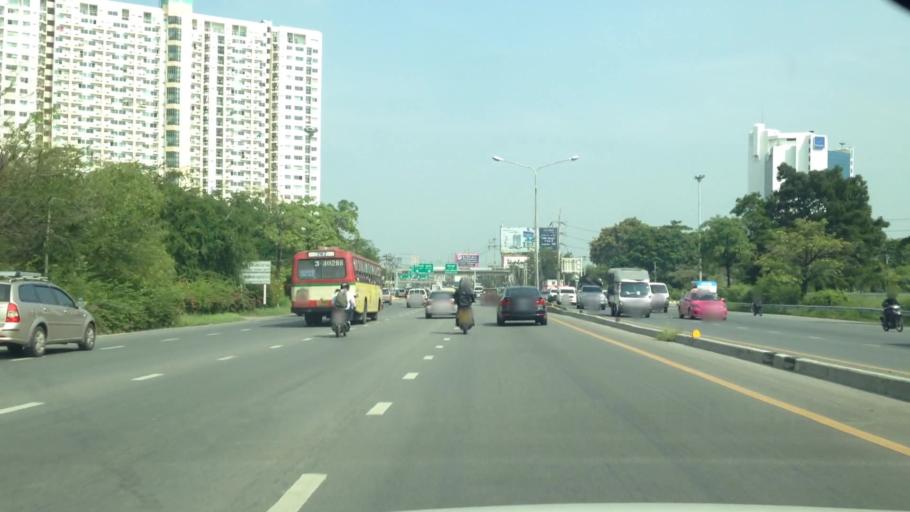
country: TH
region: Bangkok
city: Bang Na
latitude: 13.6700
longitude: 100.6452
